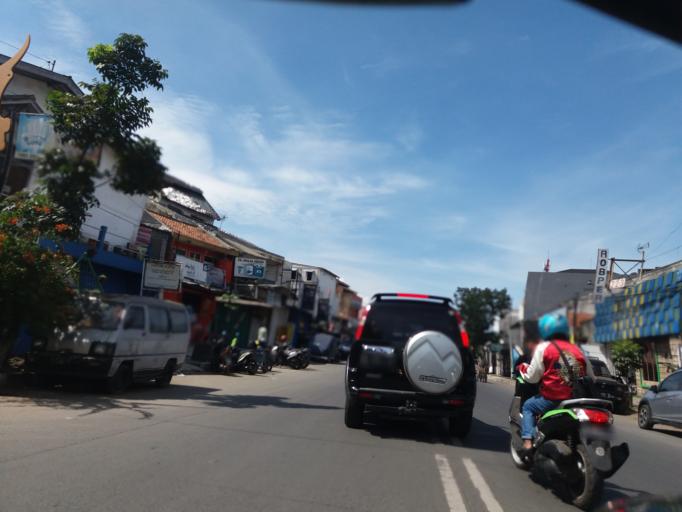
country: ID
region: West Java
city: Bandung
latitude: -6.9264
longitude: 107.5866
